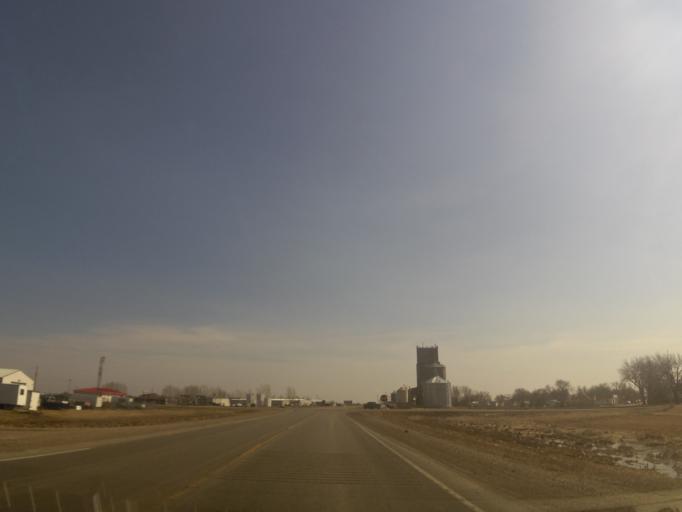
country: US
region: North Dakota
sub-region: Grand Forks County
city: Grand Forks
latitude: 48.0785
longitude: -97.1770
